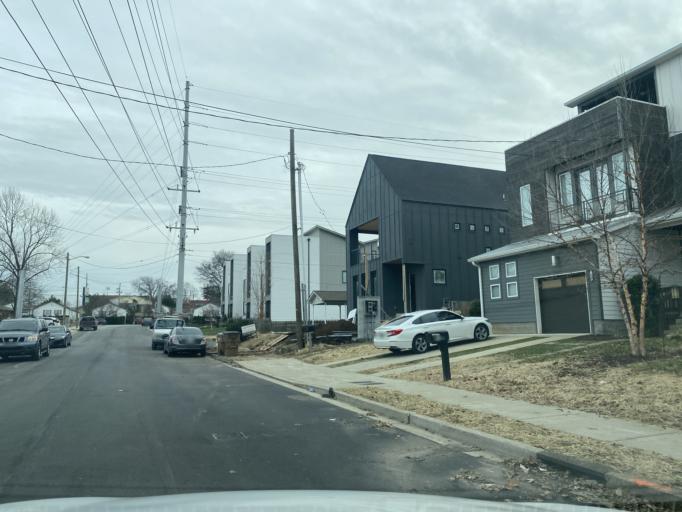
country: US
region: Tennessee
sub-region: Davidson County
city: Nashville
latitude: 36.1441
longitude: -86.7894
